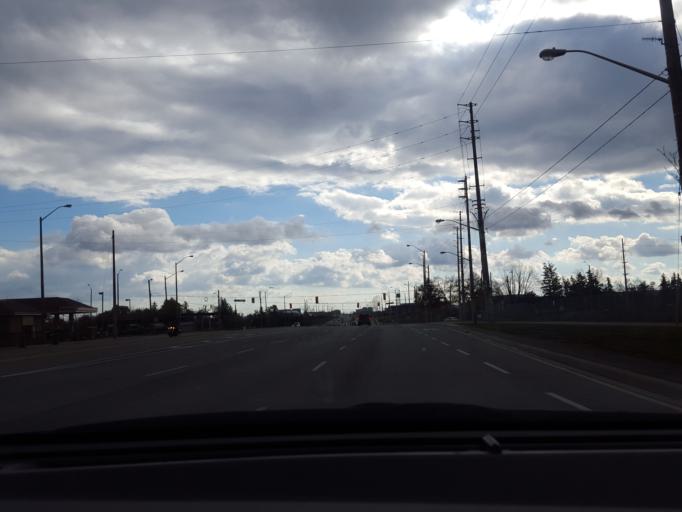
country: CA
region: Ontario
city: Brampton
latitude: 43.6285
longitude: -79.7775
